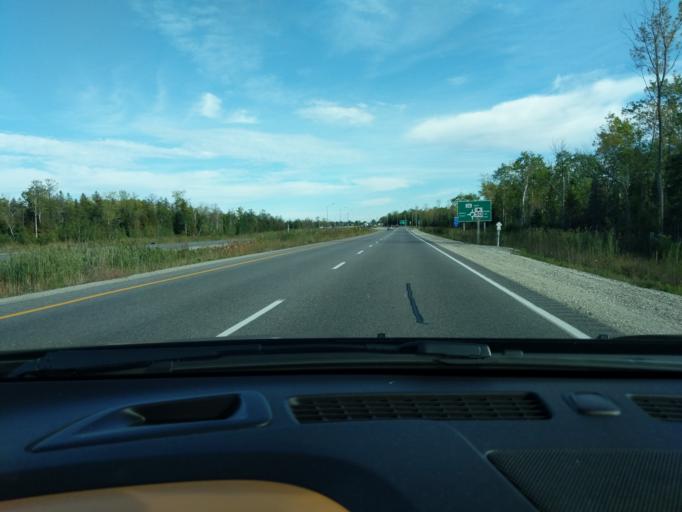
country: CA
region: Ontario
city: Collingwood
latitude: 44.4637
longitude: -80.1199
